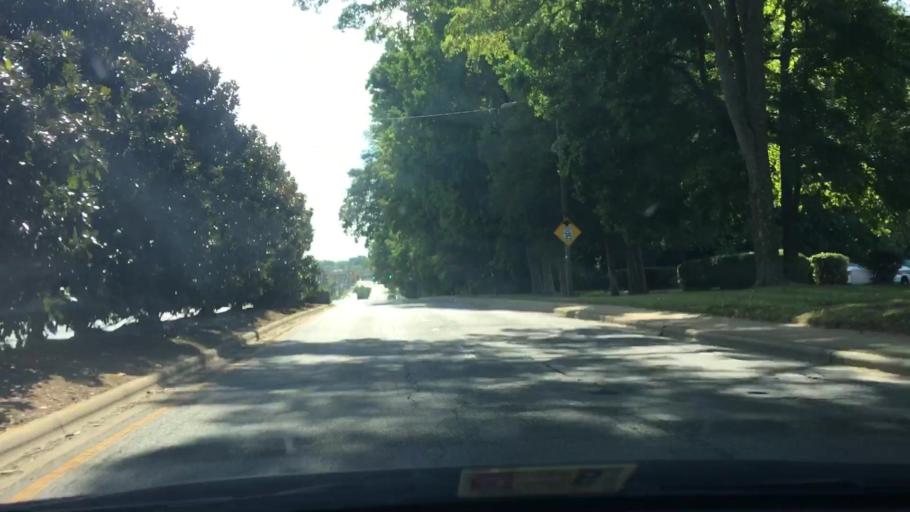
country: US
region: North Carolina
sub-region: Mecklenburg County
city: Charlotte
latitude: 35.2536
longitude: -80.8064
